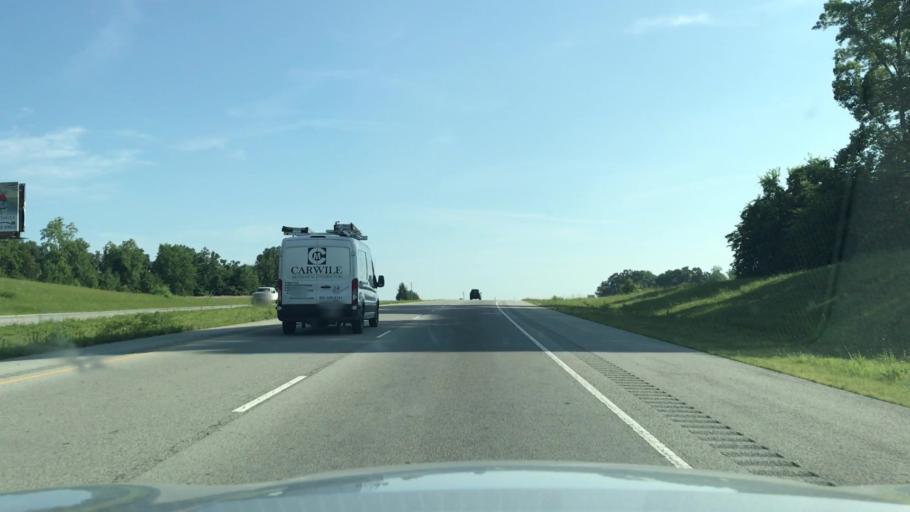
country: US
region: Tennessee
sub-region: Putnam County
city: Algood
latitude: 36.2658
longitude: -85.3909
